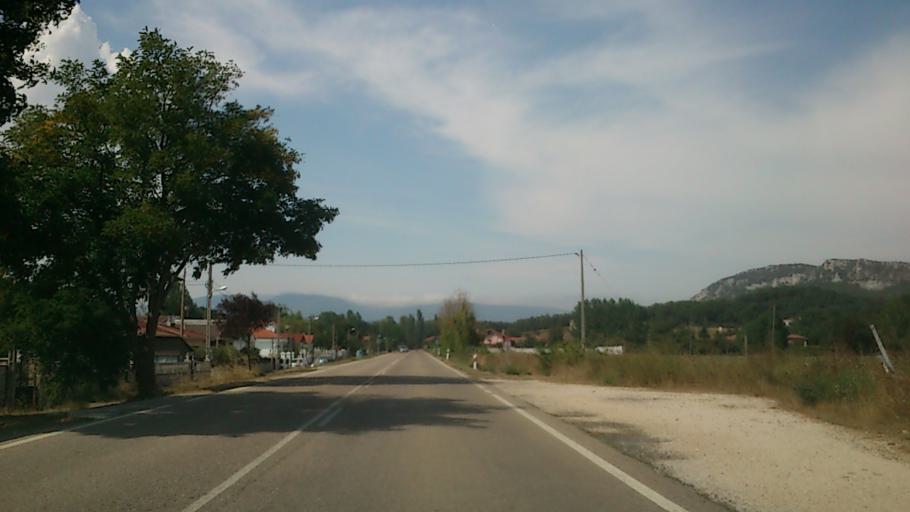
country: ES
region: Castille and Leon
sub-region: Provincia de Burgos
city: Medina de Pomar
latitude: 43.0099
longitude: -3.4822
